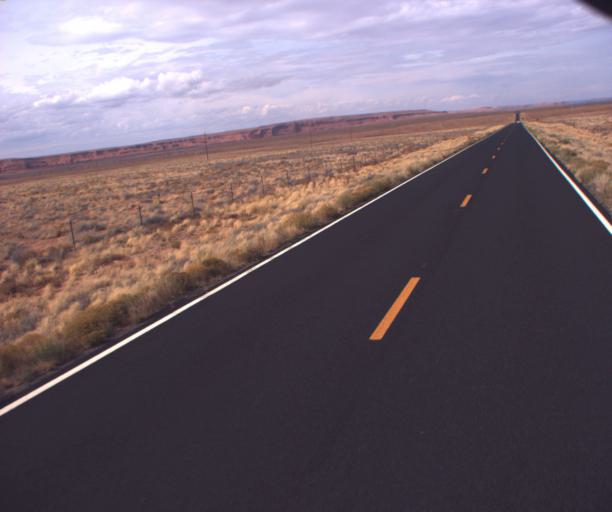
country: US
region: Arizona
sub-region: Apache County
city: Many Farms
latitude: 36.5712
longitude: -109.5478
